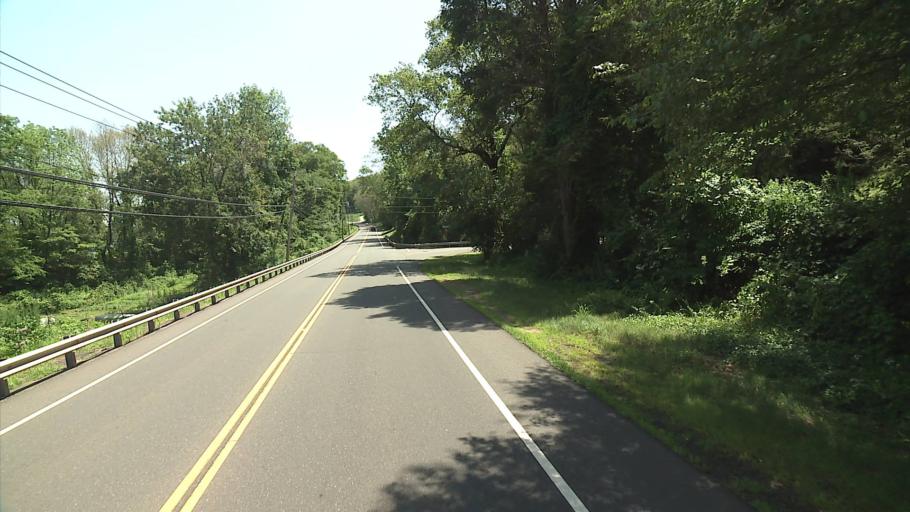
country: US
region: Connecticut
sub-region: Middlesex County
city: East Haddam
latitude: 41.4405
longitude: -72.4652
